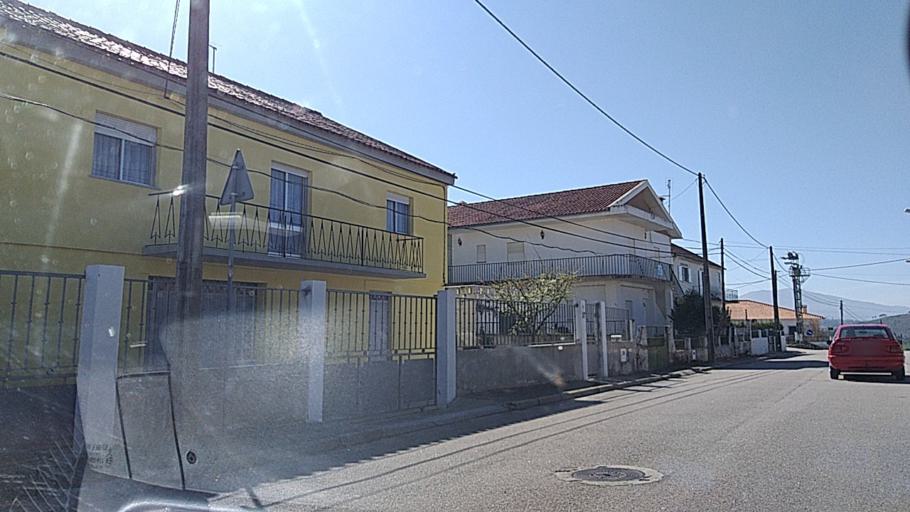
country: PT
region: Guarda
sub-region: Celorico da Beira
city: Celorico da Beira
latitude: 40.6218
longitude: -7.4057
